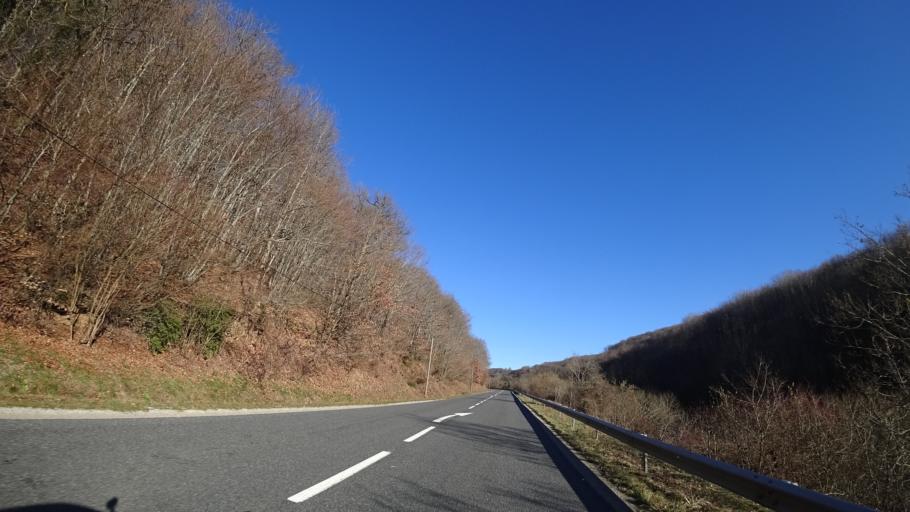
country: FR
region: Midi-Pyrenees
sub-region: Departement de l'Aveyron
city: La Loubiere
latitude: 44.3412
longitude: 2.7112
